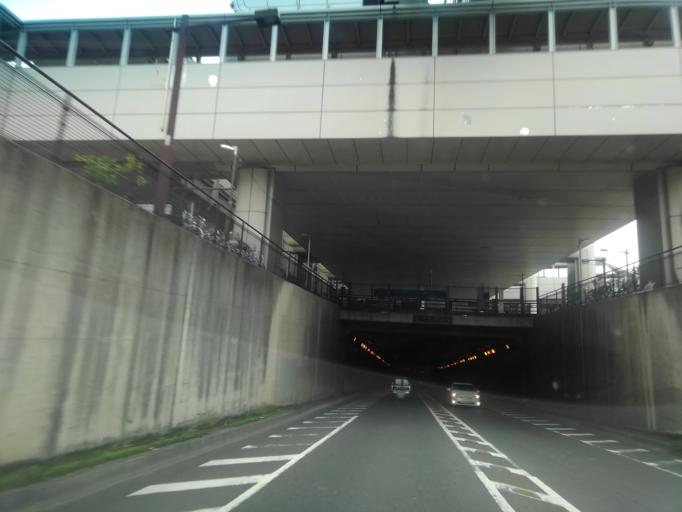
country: JP
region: Tokyo
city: Higashimurayama-shi
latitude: 35.7327
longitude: 139.4178
